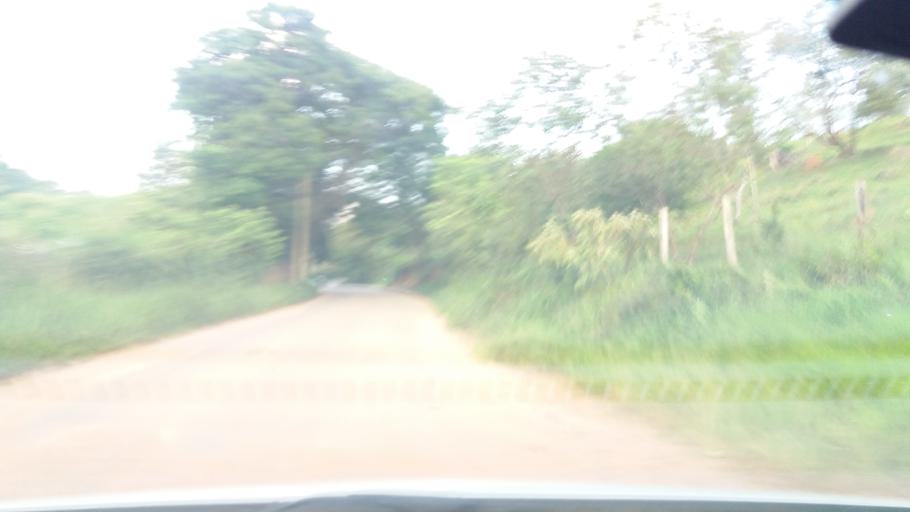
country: BR
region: Sao Paulo
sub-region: Bom Jesus Dos Perdoes
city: Bom Jesus dos Perdoes
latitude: -23.1753
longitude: -46.4831
